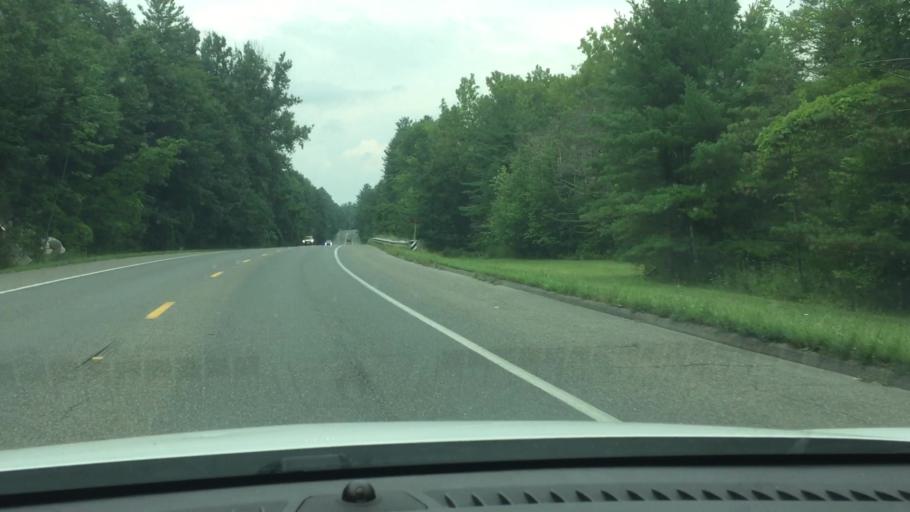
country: US
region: Massachusetts
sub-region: Berkshire County
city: Lenox
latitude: 42.3293
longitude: -73.2877
